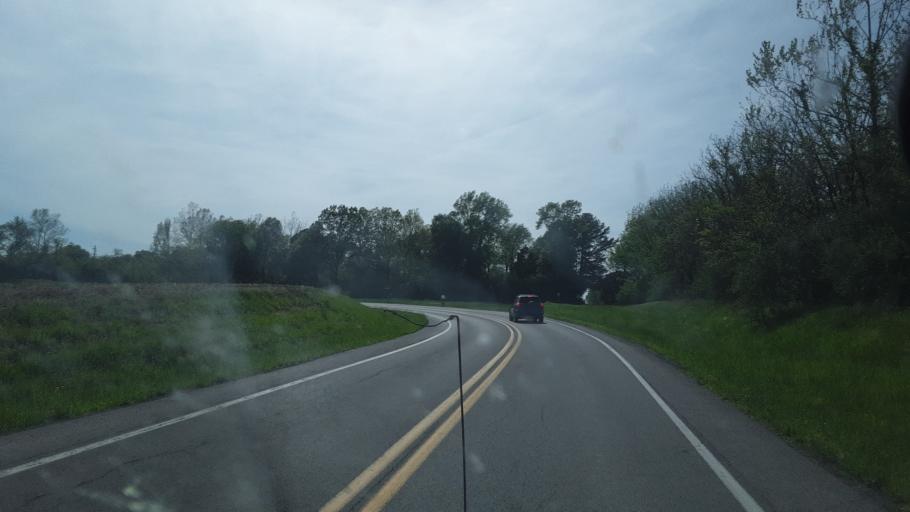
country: US
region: Illinois
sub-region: Jackson County
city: Carbondale
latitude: 37.6864
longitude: -89.2543
